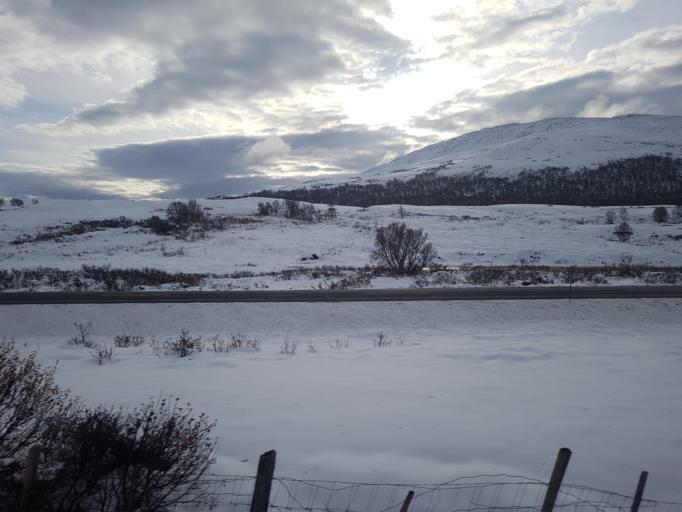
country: NO
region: Sor-Trondelag
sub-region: Oppdal
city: Oppdal
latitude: 62.4537
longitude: 9.5756
